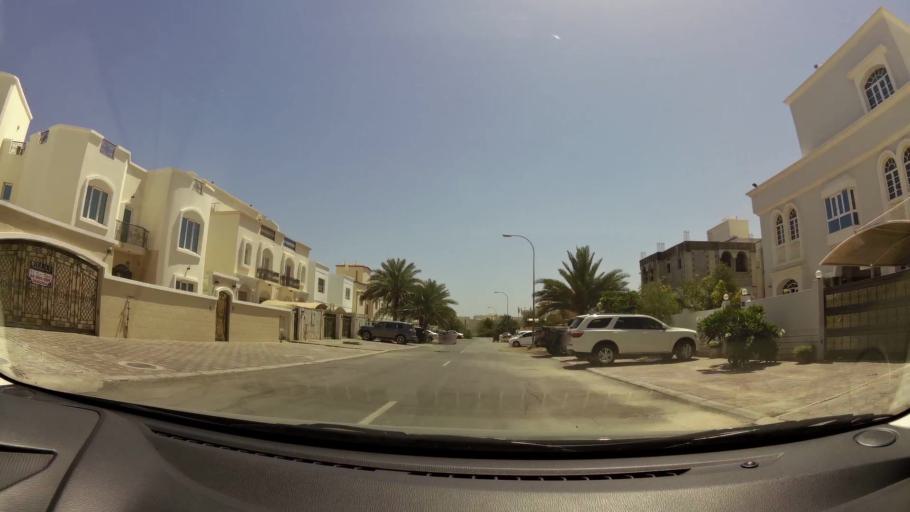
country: OM
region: Muhafazat Masqat
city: As Sib al Jadidah
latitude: 23.6212
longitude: 58.2573
